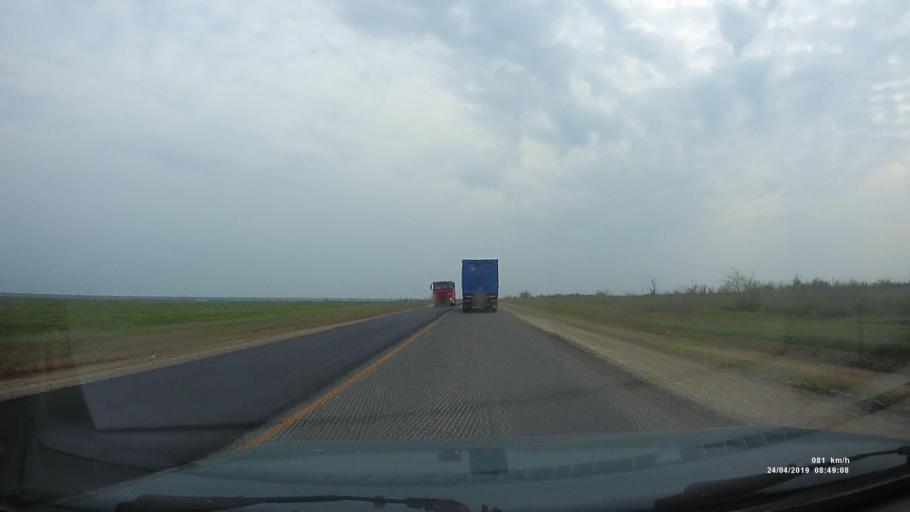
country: RU
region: Kalmykiya
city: Arshan'
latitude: 46.2552
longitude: 44.1197
